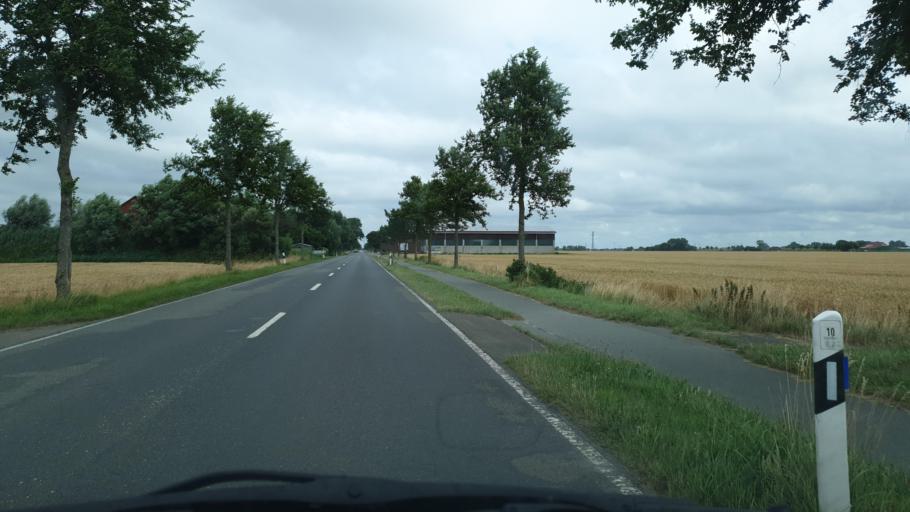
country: DE
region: Schleswig-Holstein
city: Friedrichskoog
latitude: 54.0279
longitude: 8.8484
